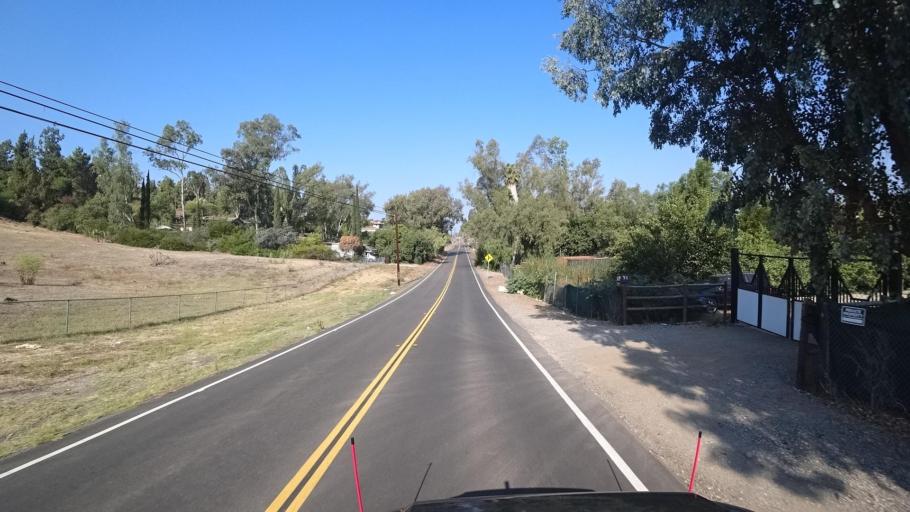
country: US
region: California
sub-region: San Diego County
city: Vista
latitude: 33.2288
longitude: -117.2339
